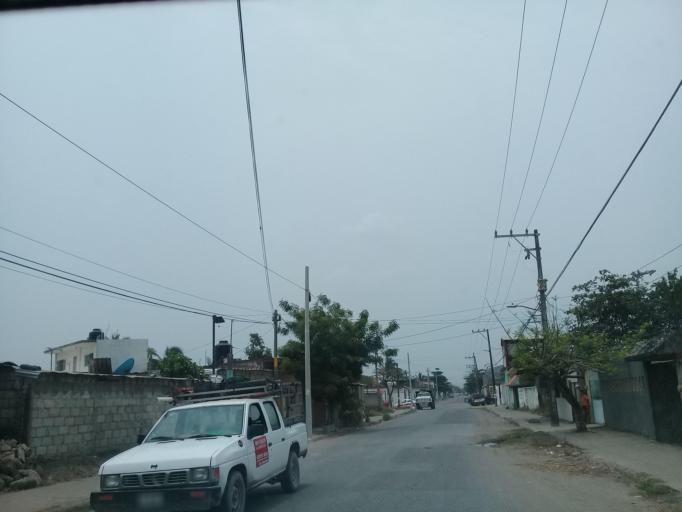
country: MX
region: Veracruz
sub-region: Veracruz
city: Las Amapolas
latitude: 19.1483
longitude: -96.2011
